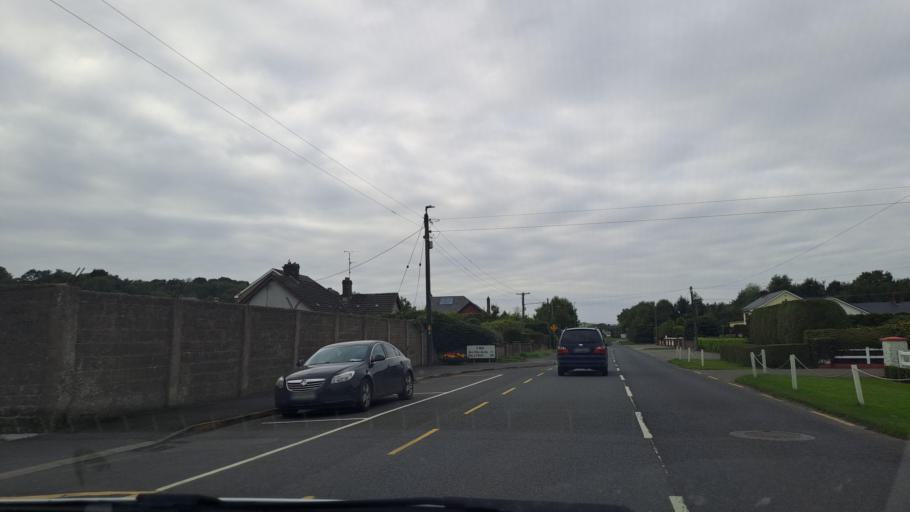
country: IE
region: Ulster
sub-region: County Monaghan
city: Carrickmacross
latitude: 53.9861
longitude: -6.7215
